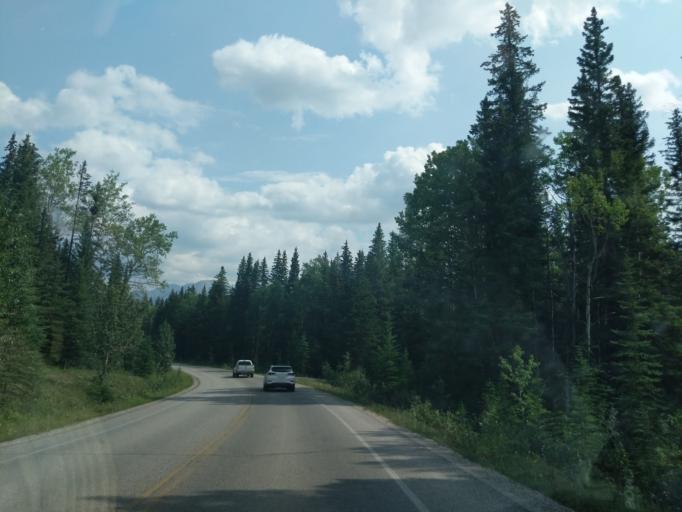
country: CA
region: Alberta
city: Banff
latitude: 51.1956
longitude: -115.7436
